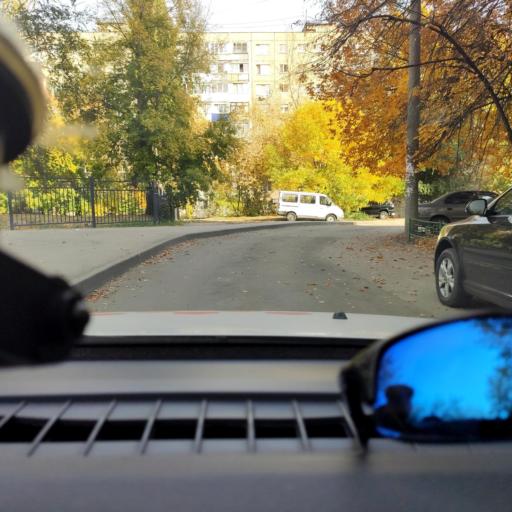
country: RU
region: Samara
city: Samara
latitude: 53.2382
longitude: 50.2205
